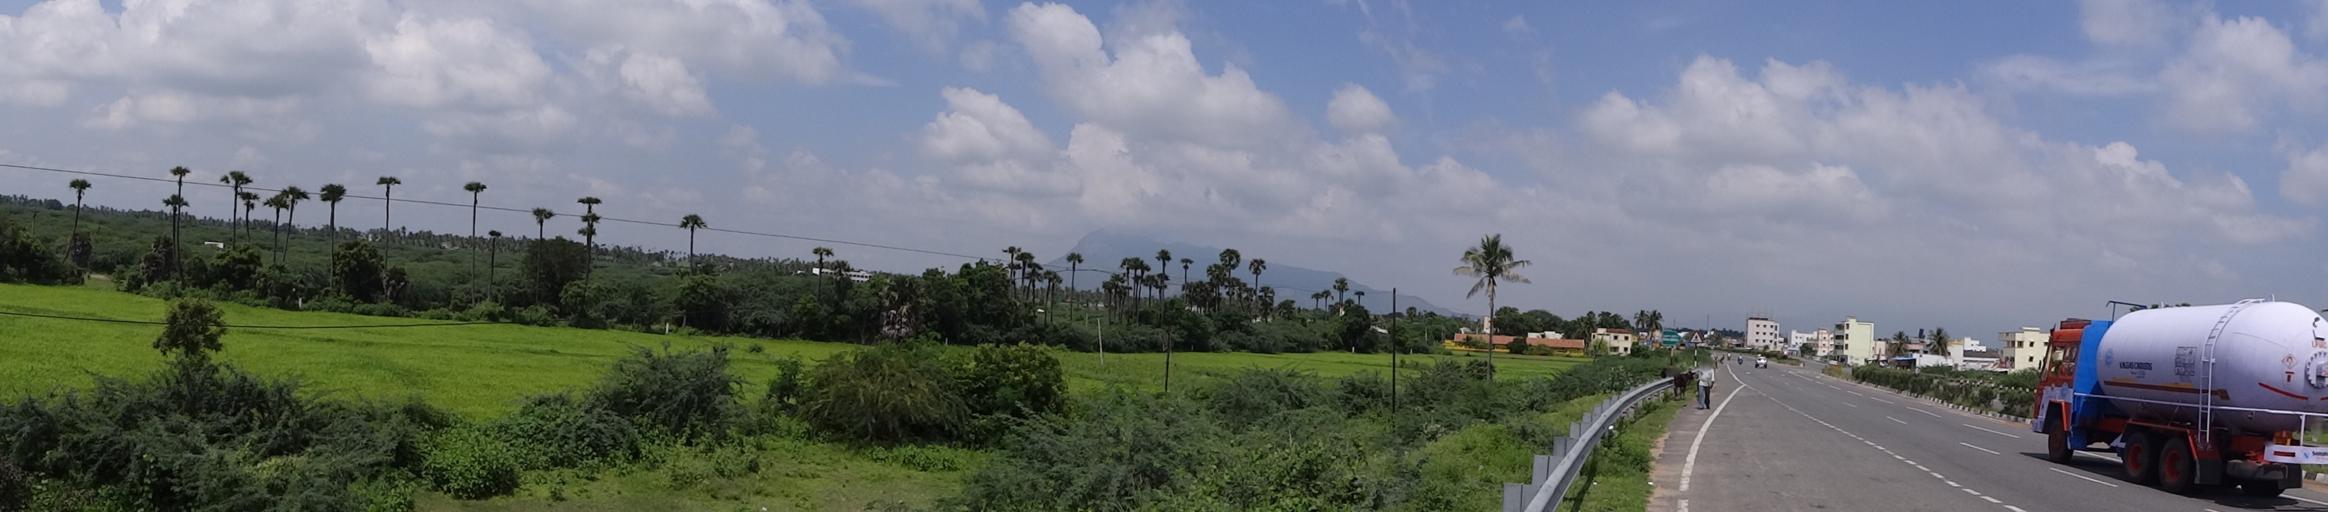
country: IN
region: Tamil Nadu
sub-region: Namakkal
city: Rasipuram
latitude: 11.3847
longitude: 78.1607
